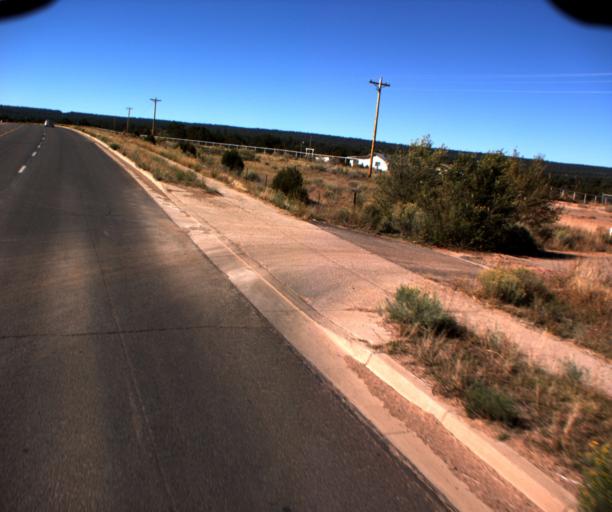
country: US
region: Arizona
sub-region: Apache County
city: Saint Michaels
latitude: 35.6588
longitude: -109.1150
